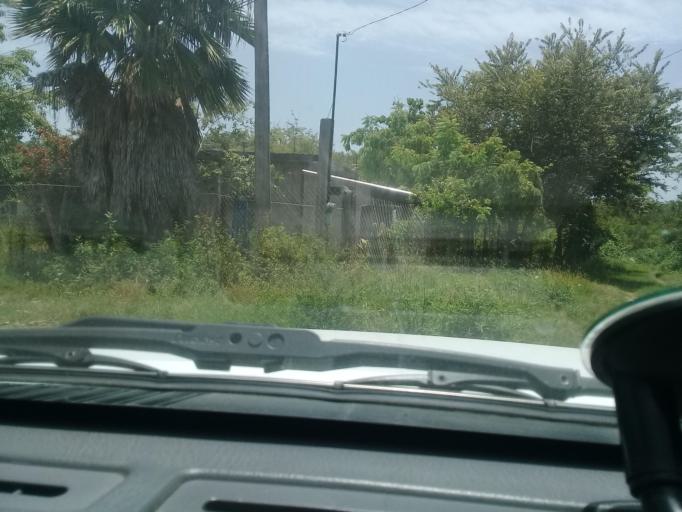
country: MX
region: Veracruz
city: Anahuac
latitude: 22.2243
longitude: -97.8175
